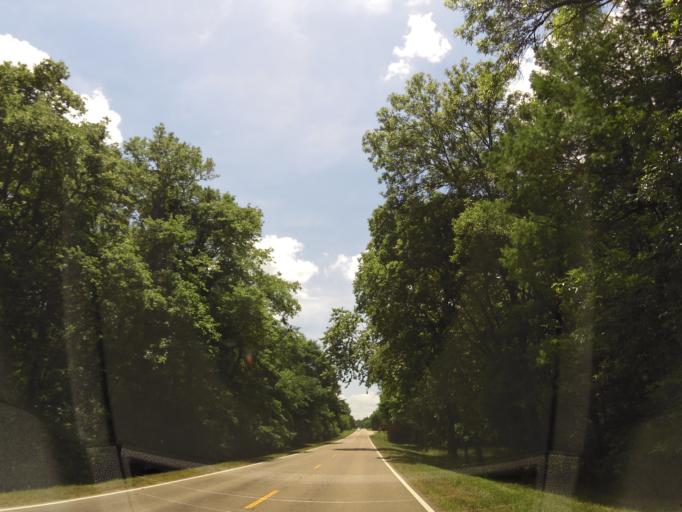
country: US
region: Mississippi
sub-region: Lee County
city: Tupelo
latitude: 34.2768
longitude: -88.7382
